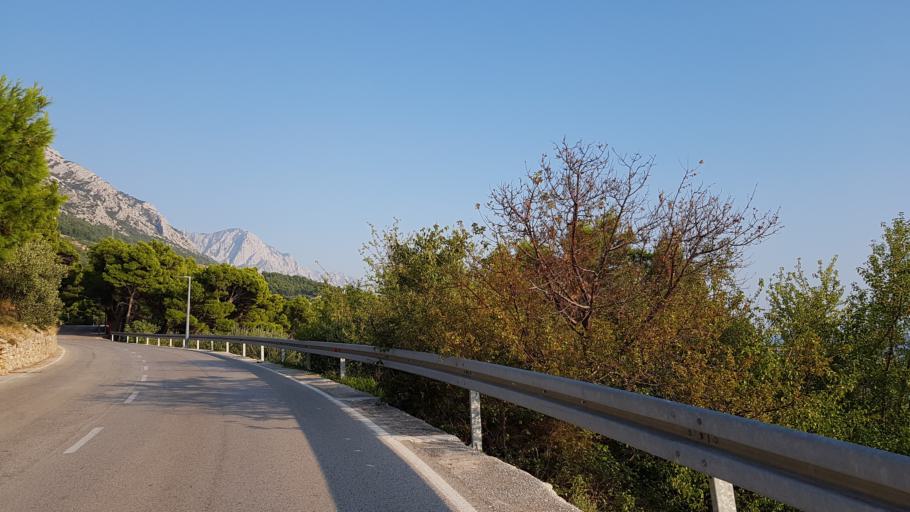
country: HR
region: Splitsko-Dalmatinska
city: Donja Brela
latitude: 43.3825
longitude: 16.9139
